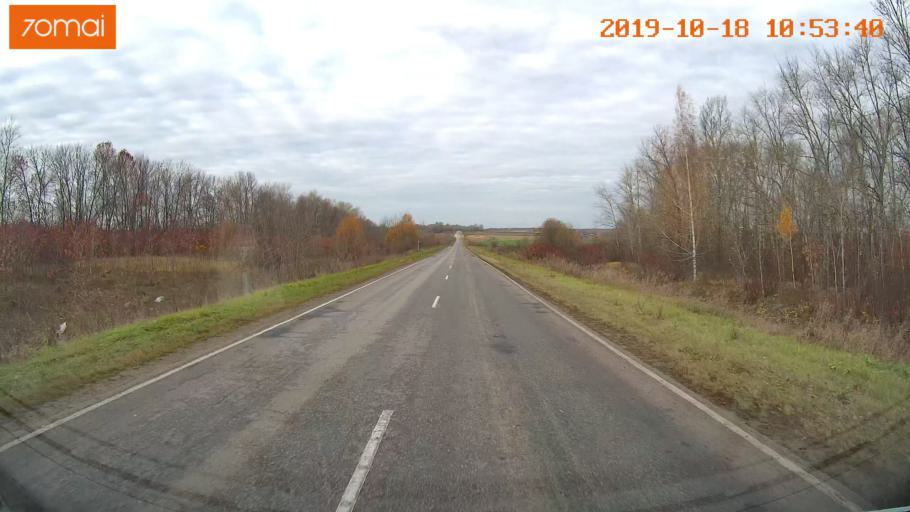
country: RU
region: Tula
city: Yepifan'
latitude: 53.7813
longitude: 38.6334
